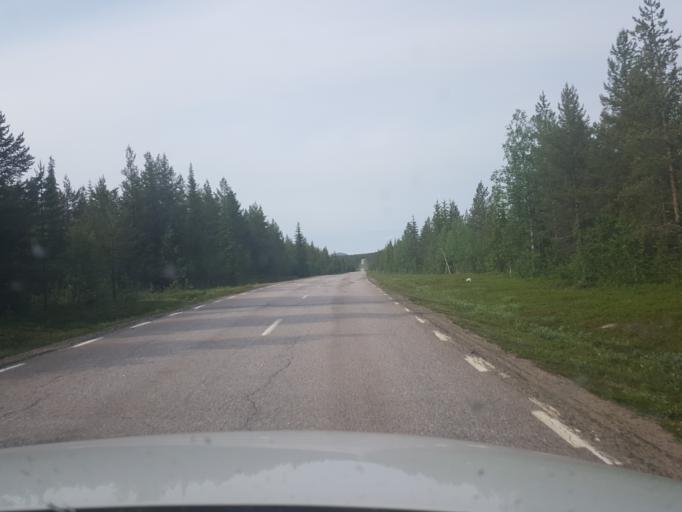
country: SE
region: Norrbotten
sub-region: Arjeplogs Kommun
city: Arjeplog
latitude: 65.7851
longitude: 18.0077
